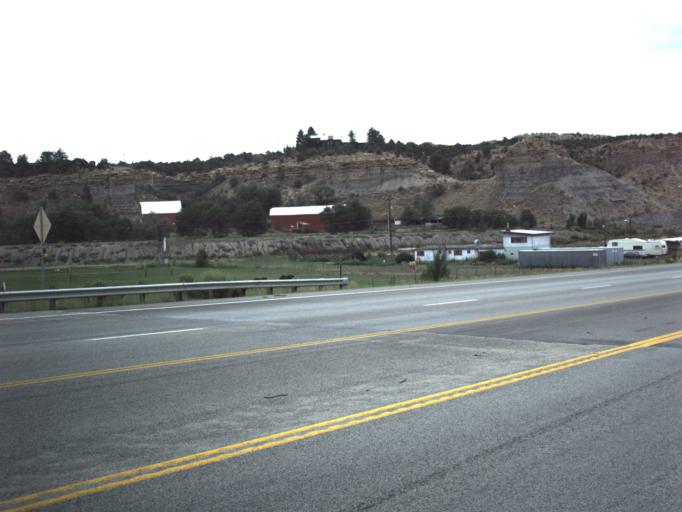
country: US
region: Utah
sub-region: Carbon County
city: Spring Glen
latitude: 39.6497
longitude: -110.8603
